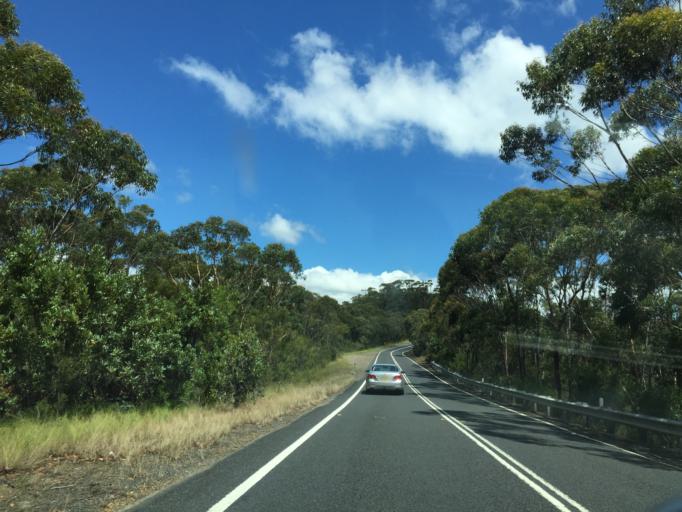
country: AU
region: New South Wales
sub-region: Blue Mountains Municipality
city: Blackheath
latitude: -33.5576
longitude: 150.3744
